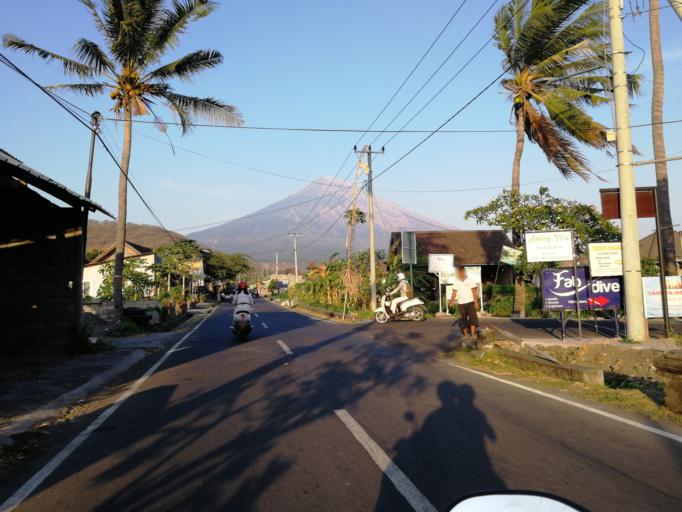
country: ID
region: Bali
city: Biaslantang Kaler
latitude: -8.3359
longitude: 115.6316
